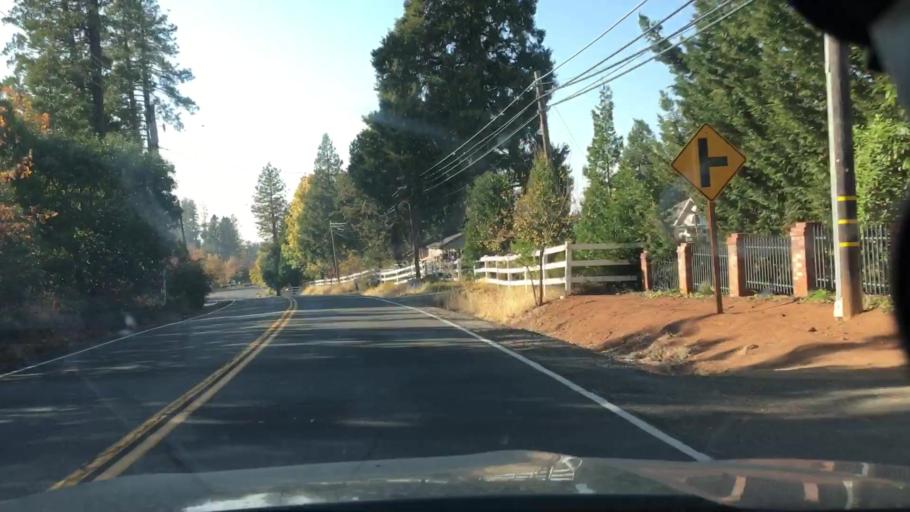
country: US
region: California
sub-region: El Dorado County
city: Camino
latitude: 38.7409
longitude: -120.6931
